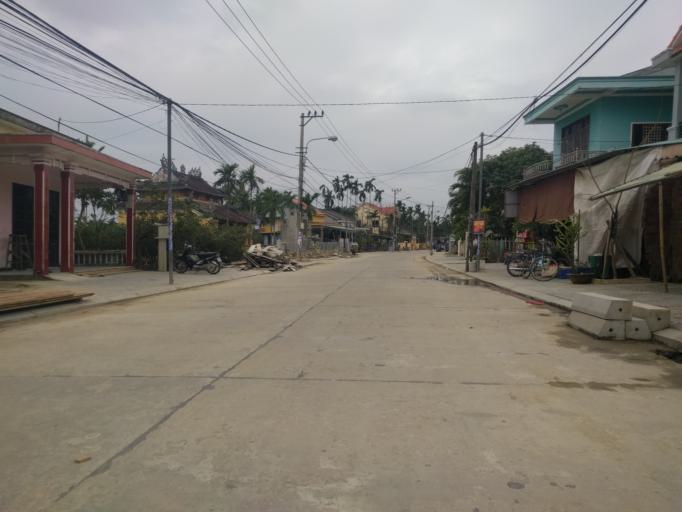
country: VN
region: Quang Nam
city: Hoi An
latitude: 15.8698
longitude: 108.3489
